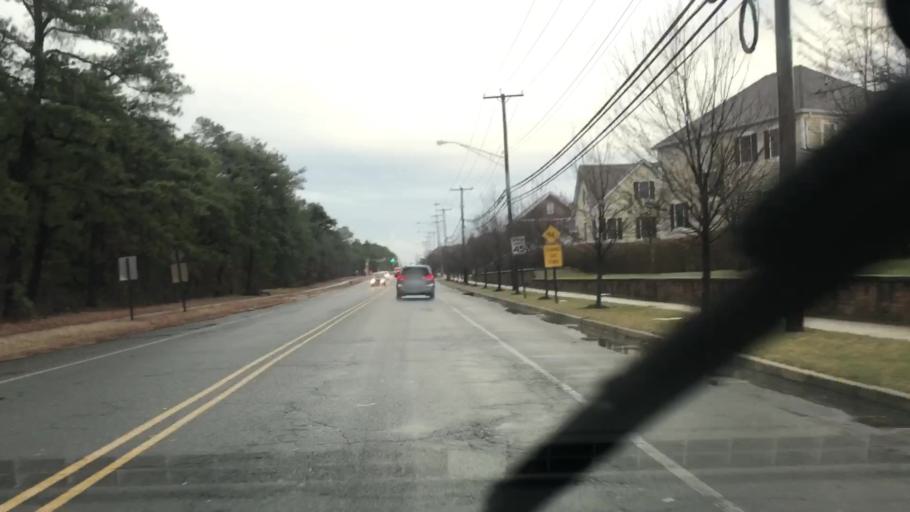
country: US
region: New Jersey
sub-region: Ocean County
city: Lakewood
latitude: 40.0747
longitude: -74.2048
